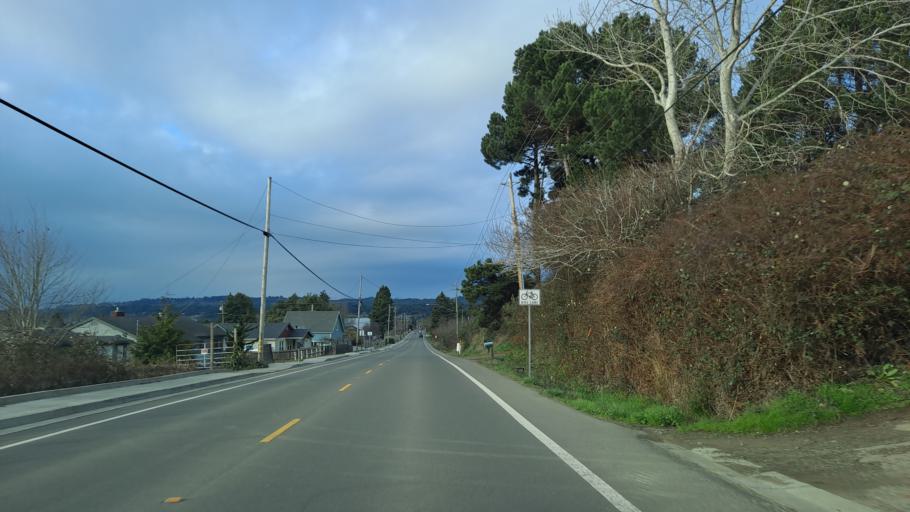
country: US
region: California
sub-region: Humboldt County
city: Fortuna
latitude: 40.5729
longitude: -124.1276
